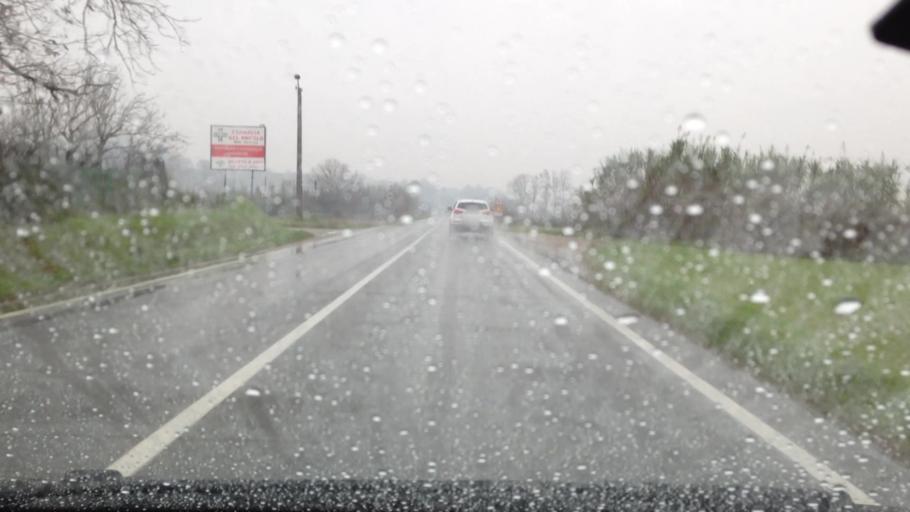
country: IT
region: Piedmont
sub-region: Provincia di Asti
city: Rocca d'Arazzo
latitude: 44.9010
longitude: 8.2914
